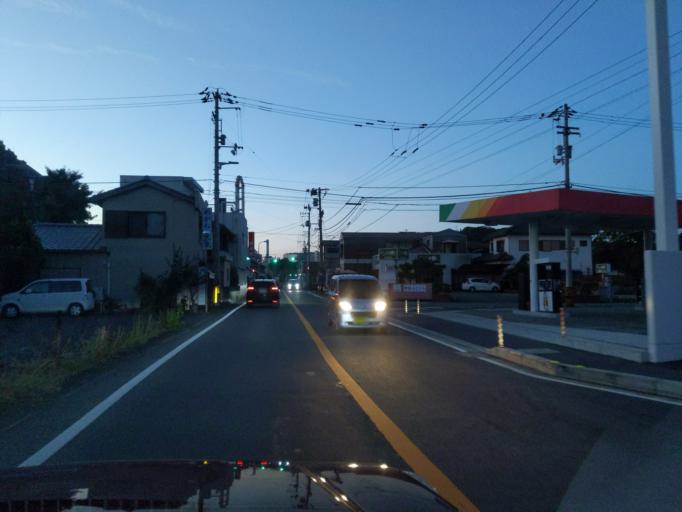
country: JP
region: Tokushima
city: Anan
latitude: 33.8875
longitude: 134.6528
